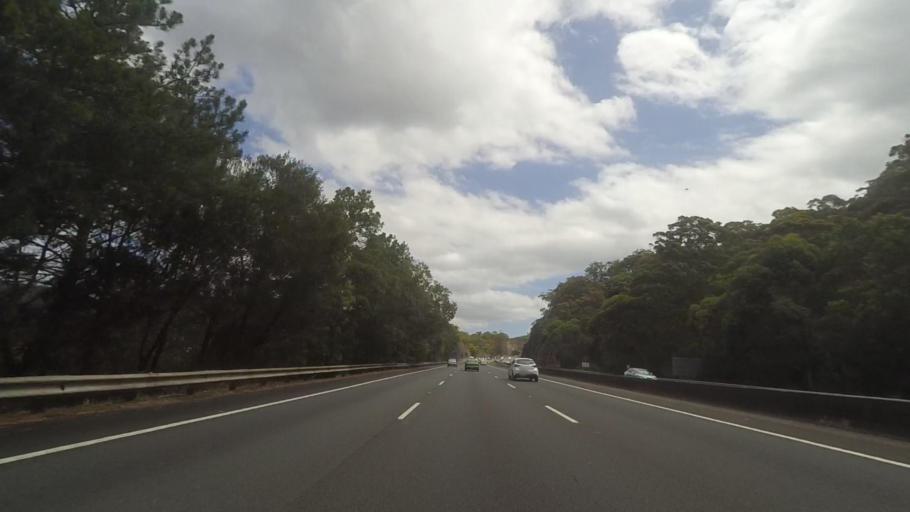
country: AU
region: New South Wales
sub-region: Hornsby Shire
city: Berowra
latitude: -33.5432
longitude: 151.1977
